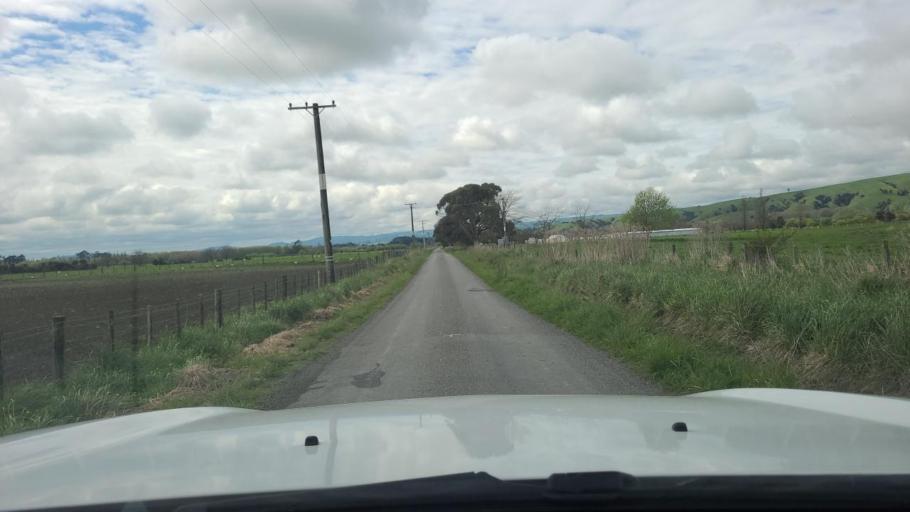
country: NZ
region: Wellington
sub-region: Masterton District
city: Masterton
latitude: -41.0956
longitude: 175.4879
